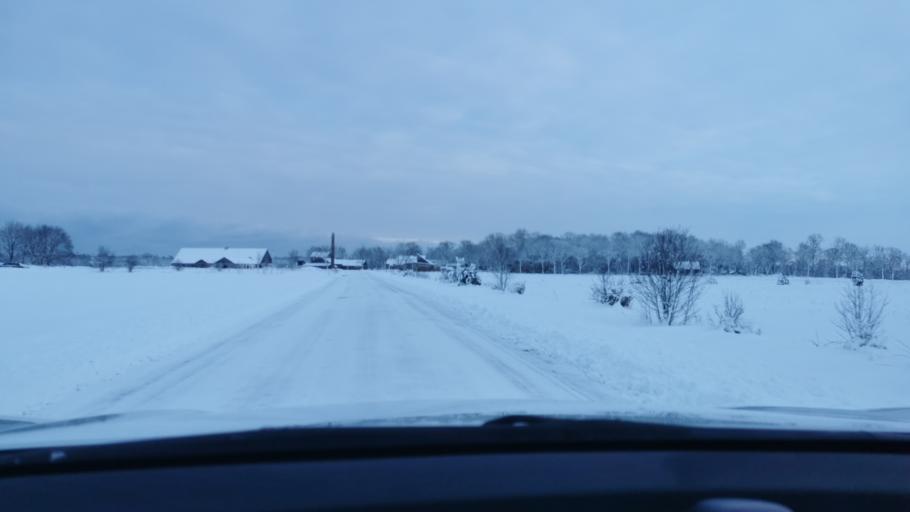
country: EE
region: Laeaene-Virumaa
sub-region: Viru-Nigula vald
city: Kunda
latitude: 59.4922
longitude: 26.4005
